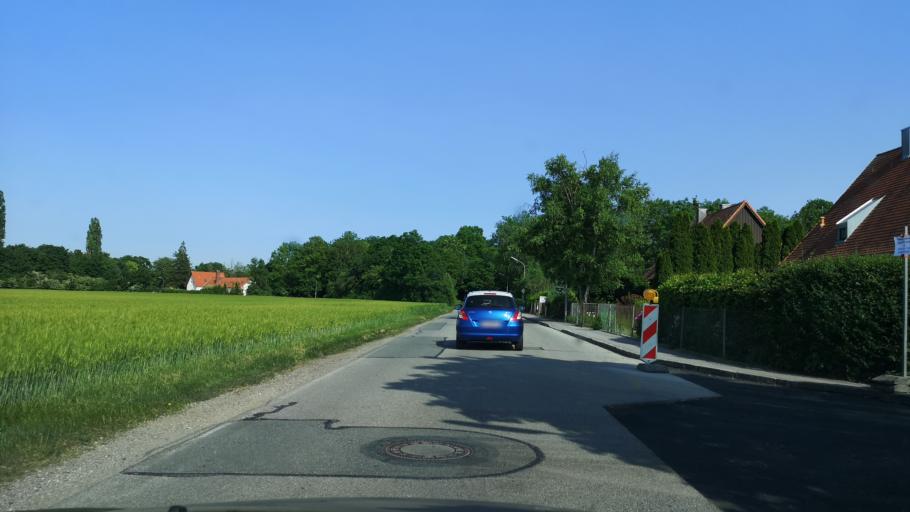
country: DE
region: Bavaria
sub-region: Upper Bavaria
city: Kirchheim bei Muenchen
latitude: 48.1718
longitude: 11.7746
